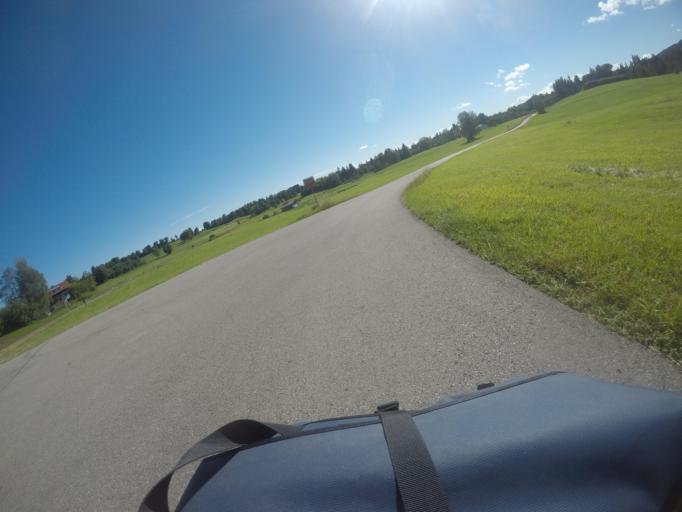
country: DE
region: Bavaria
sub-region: Swabia
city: Oy-Mittelberg
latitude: 47.6283
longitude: 10.4659
